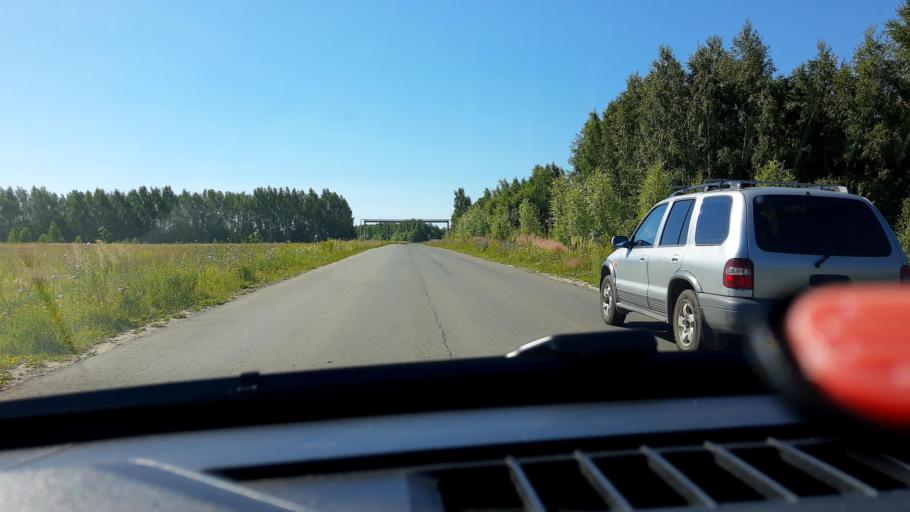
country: RU
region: Nizjnij Novgorod
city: Babino
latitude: 56.1366
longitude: 43.6424
